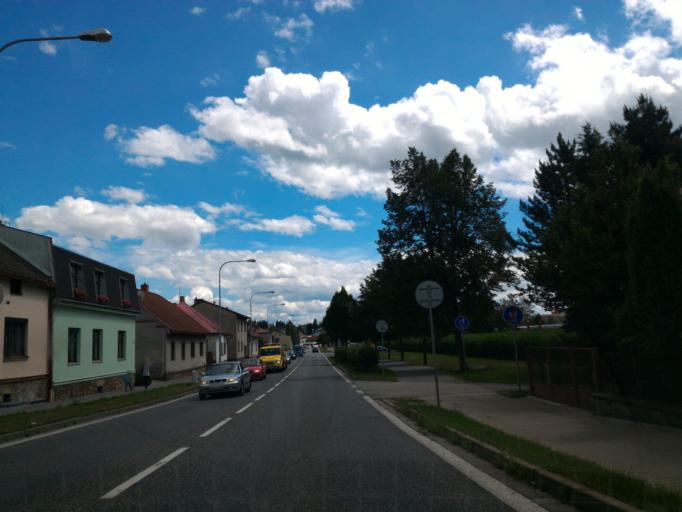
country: CZ
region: Vysocina
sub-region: Okres Zd'ar nad Sazavou
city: Zd'ar nad Sazavou
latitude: 49.5742
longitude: 15.9405
